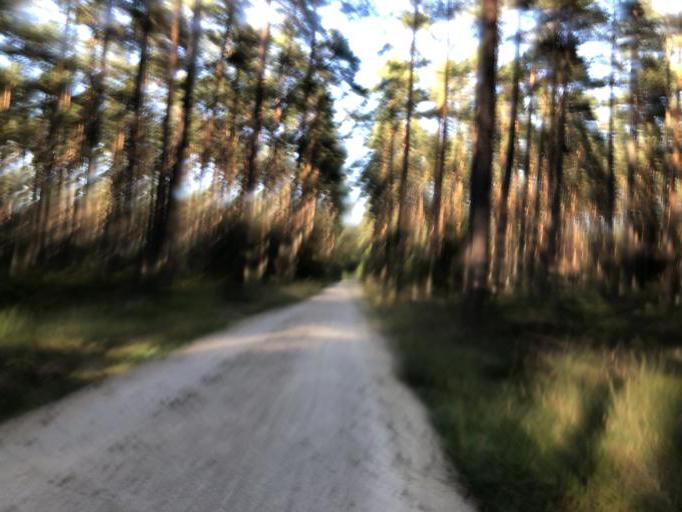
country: DE
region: Bavaria
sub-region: Regierungsbezirk Mittelfranken
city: Uttenreuth
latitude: 49.5707
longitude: 11.0812
